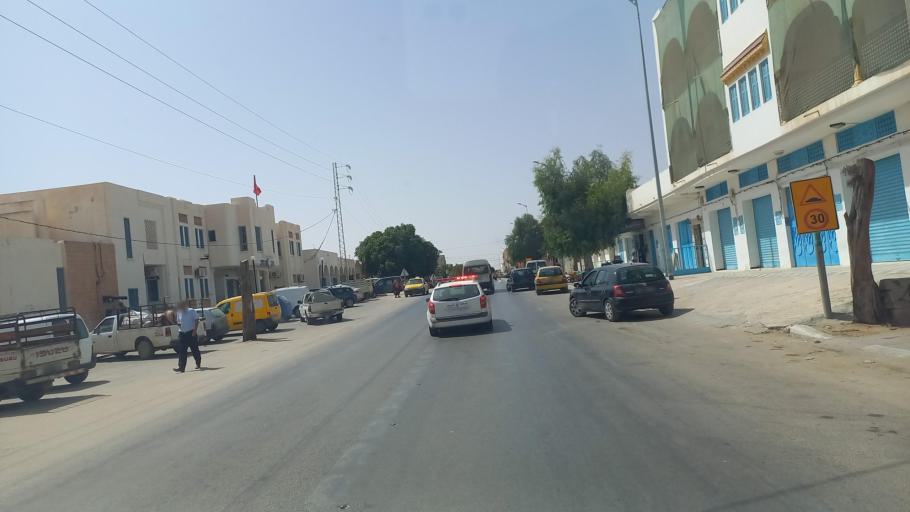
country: TN
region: Madanin
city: Medenine
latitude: 33.3276
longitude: 10.4847
